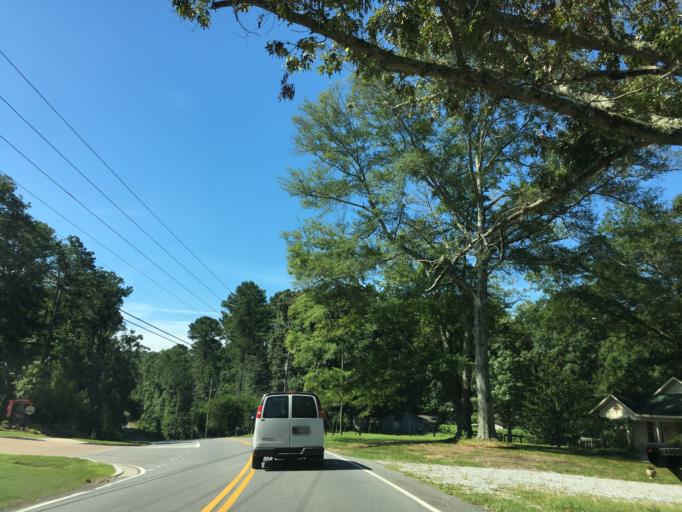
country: US
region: Georgia
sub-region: Fulton County
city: Milton
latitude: 34.1445
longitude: -84.2870
